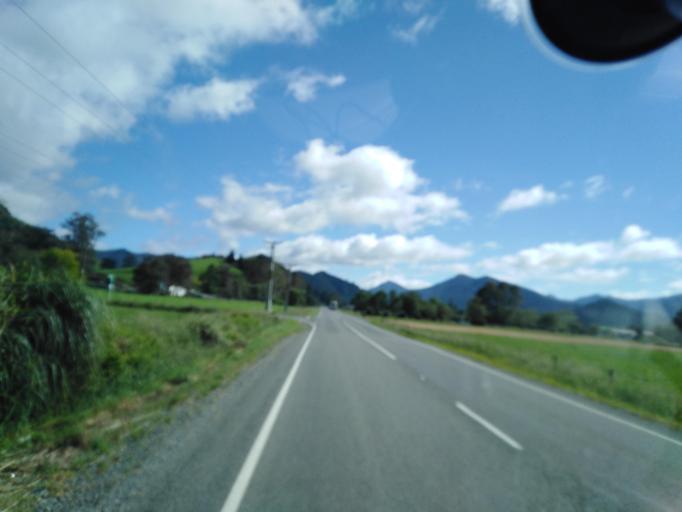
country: NZ
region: Nelson
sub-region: Nelson City
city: Nelson
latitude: -41.2395
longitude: 173.5793
